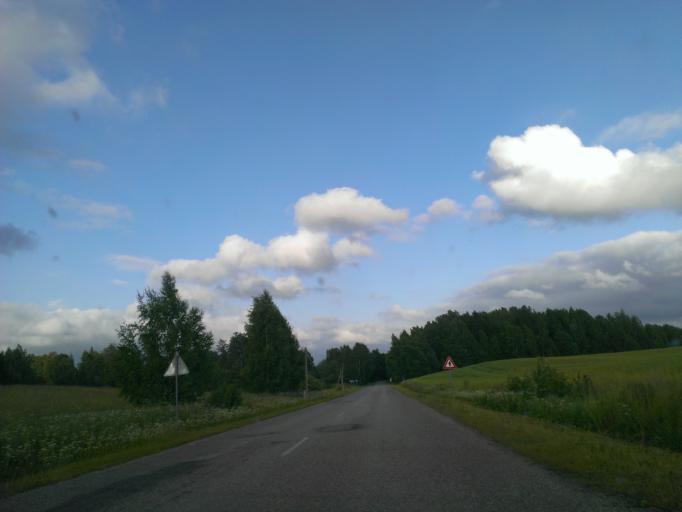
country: LV
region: Skrunda
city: Skrunda
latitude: 56.6902
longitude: 21.8741
